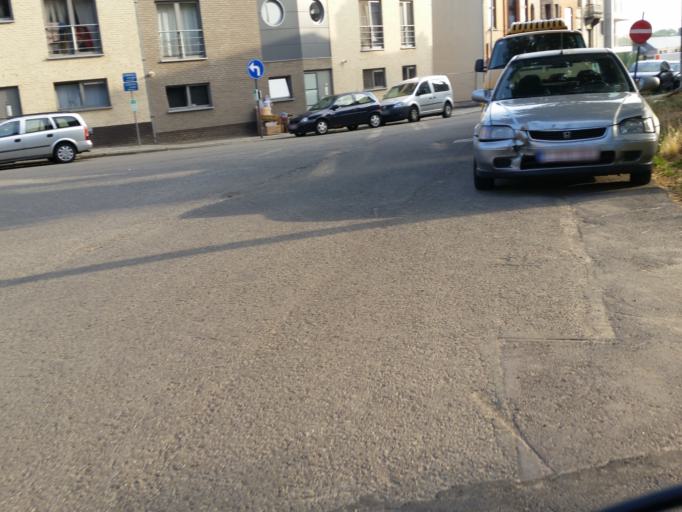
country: BE
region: Flanders
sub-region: Provincie Vlaams-Brabant
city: Vilvoorde
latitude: 50.9246
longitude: 4.4163
